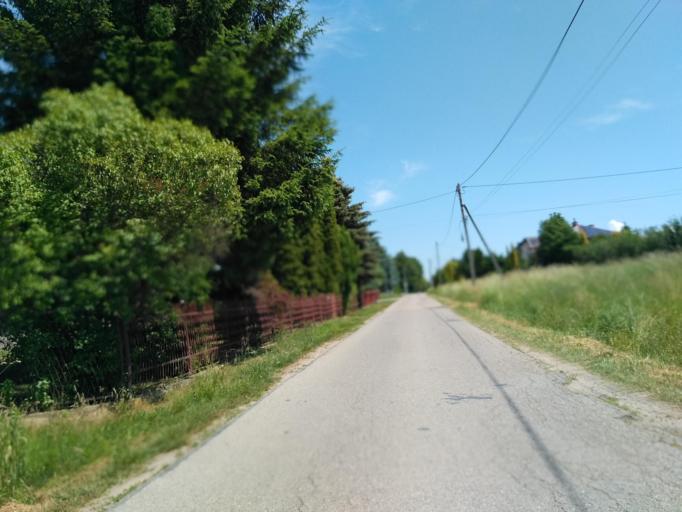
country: PL
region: Subcarpathian Voivodeship
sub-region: Powiat krosnienski
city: Korczyna
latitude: 49.7066
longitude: 21.7961
